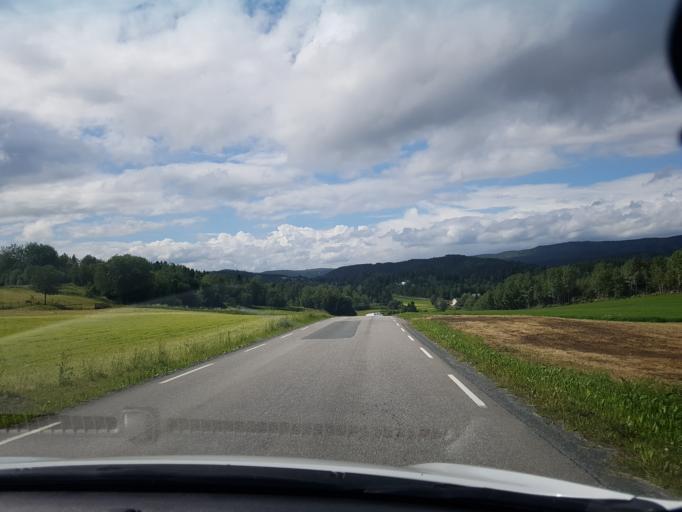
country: NO
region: Nord-Trondelag
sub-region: Stjordal
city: Stjordalshalsen
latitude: 63.5926
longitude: 10.9820
